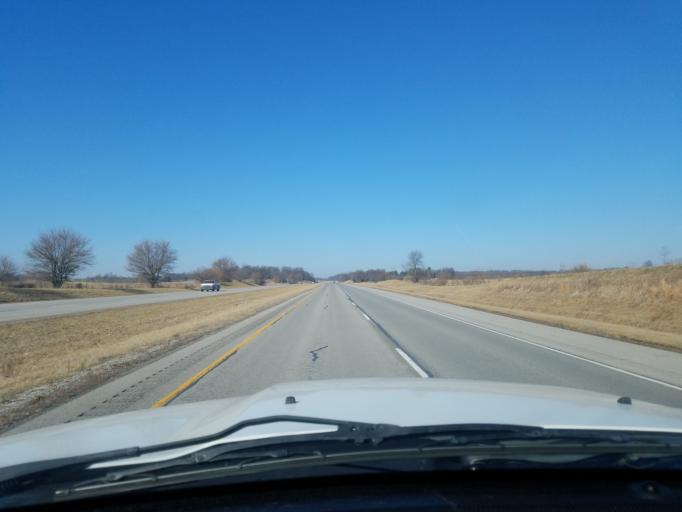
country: US
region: Kentucky
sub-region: Larue County
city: Hodgenville
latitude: 37.6140
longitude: -85.8042
